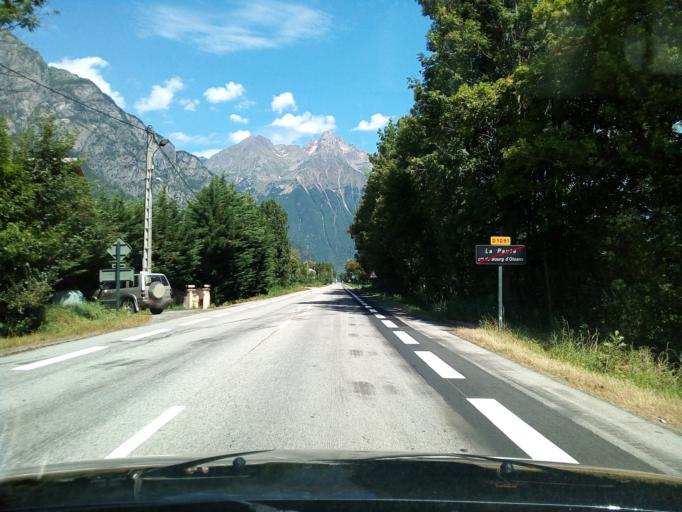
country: FR
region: Rhone-Alpes
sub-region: Departement de l'Isere
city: Huez
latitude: 45.0815
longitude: 6.0135
